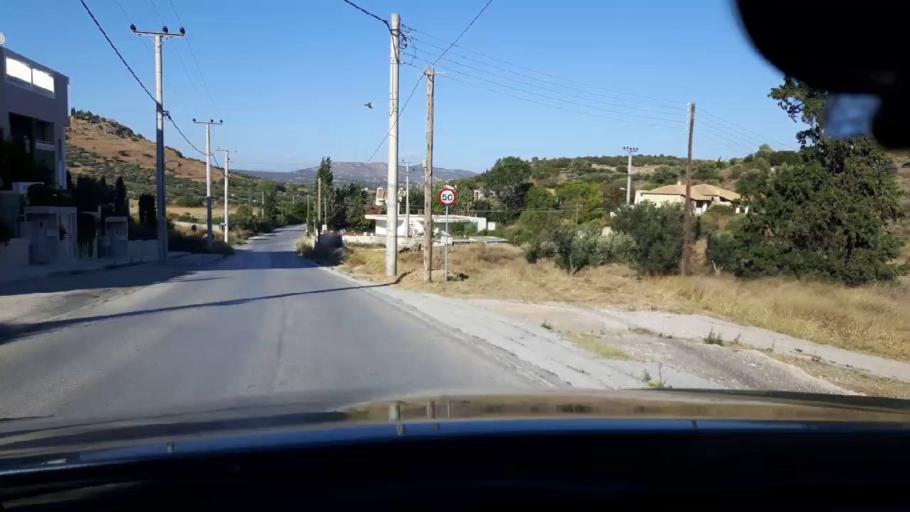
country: GR
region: Attica
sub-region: Nomarchia Anatolikis Attikis
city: Markopoulo
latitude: 37.8829
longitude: 23.9448
